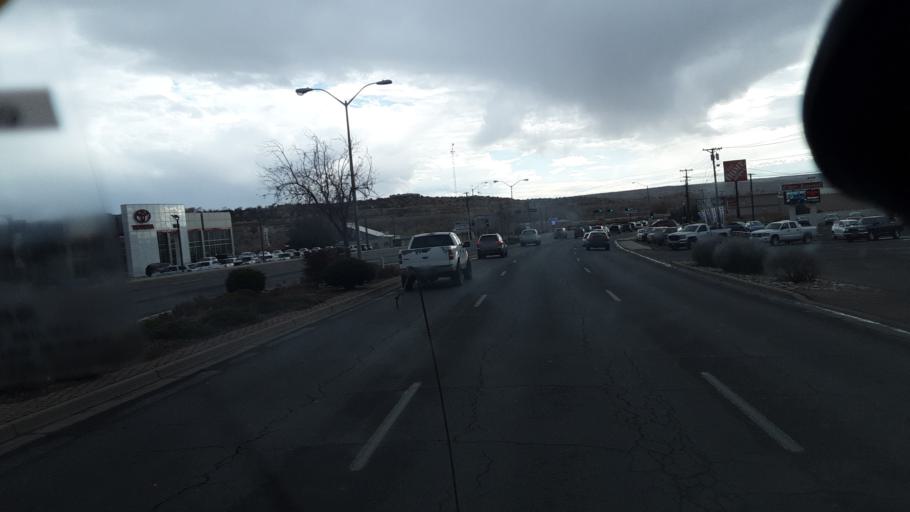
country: US
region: New Mexico
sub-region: San Juan County
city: Farmington
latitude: 36.7542
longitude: -108.1569
